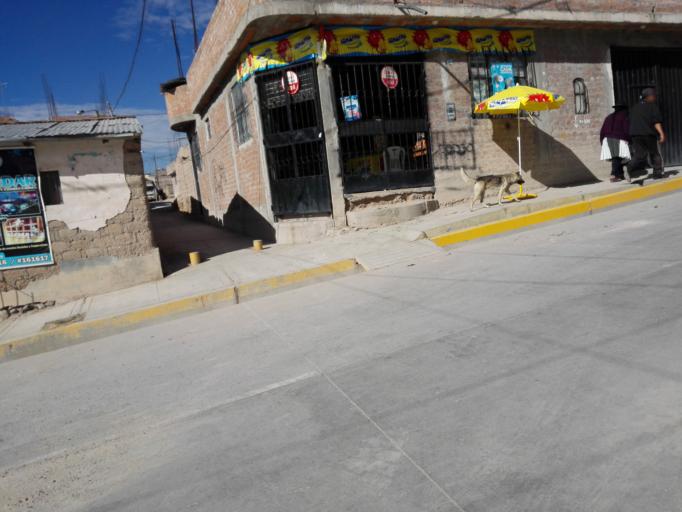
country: PE
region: Ayacucho
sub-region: Provincia de Huamanga
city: Ayacucho
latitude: -13.1368
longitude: -74.2334
